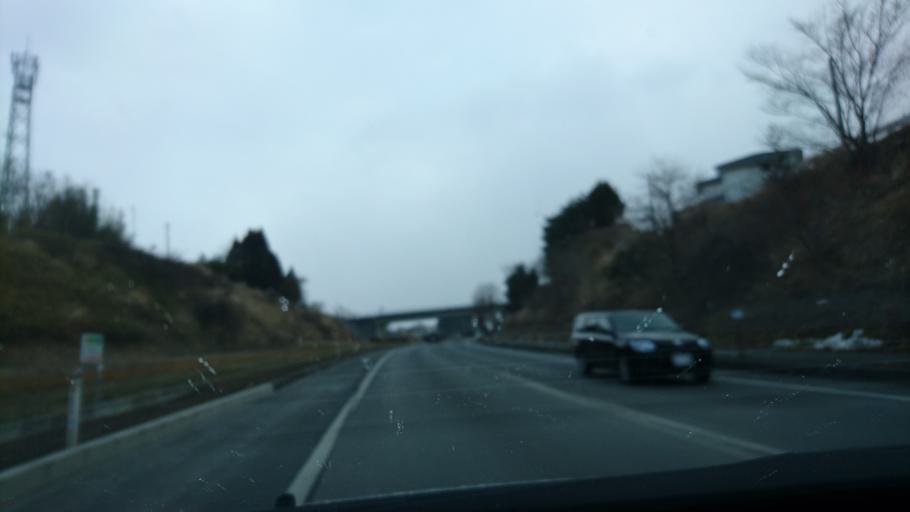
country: JP
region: Iwate
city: Ofunato
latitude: 38.8854
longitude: 141.5658
